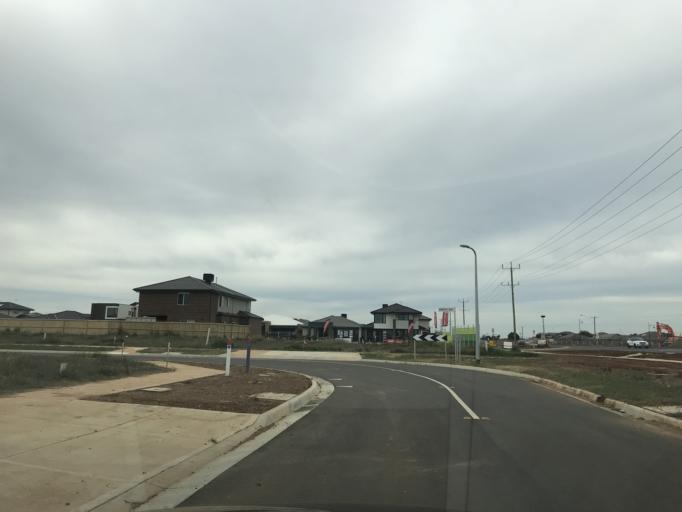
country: AU
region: Victoria
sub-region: Wyndham
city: Williams Landing
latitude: -37.8368
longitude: 144.7219
